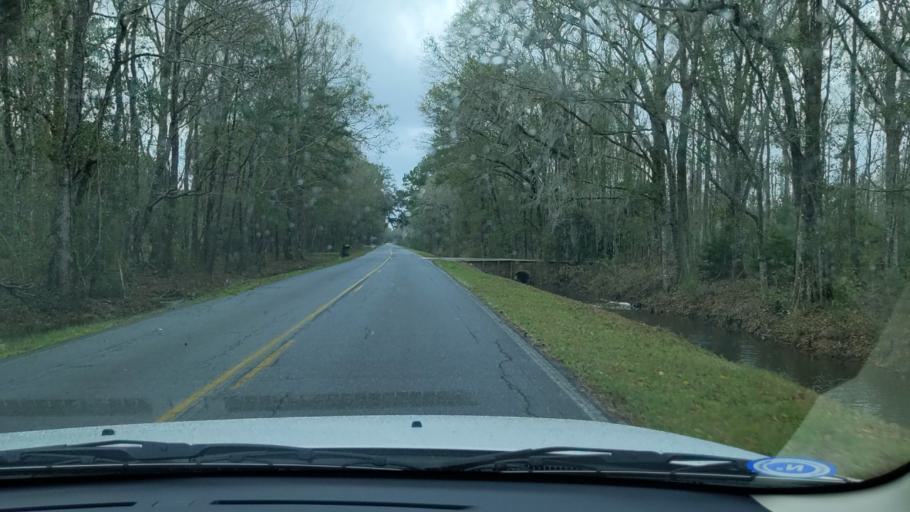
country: US
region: Georgia
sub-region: Bryan County
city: Richmond Hill
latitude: 32.0321
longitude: -81.3092
